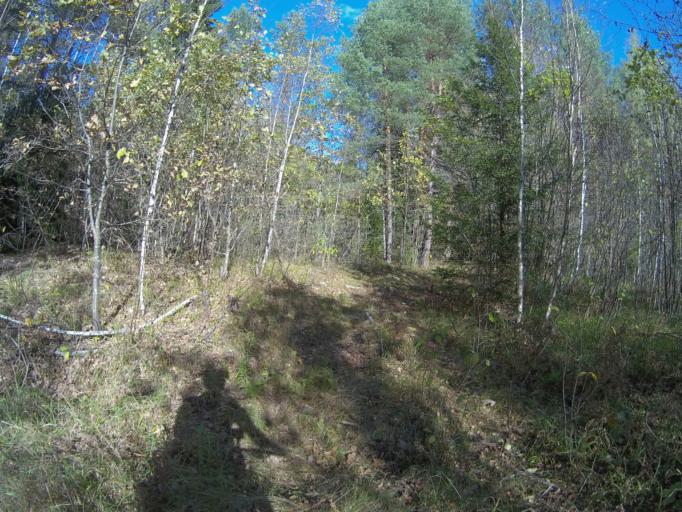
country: RU
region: Vladimir
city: Golovino
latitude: 56.0193
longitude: 40.4802
